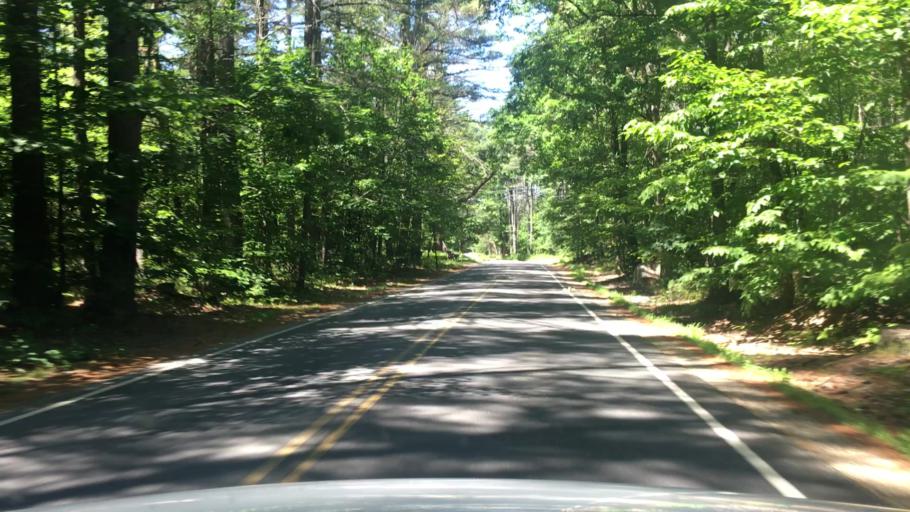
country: US
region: New Hampshire
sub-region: Merrimack County
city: Hopkinton
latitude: 43.2322
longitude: -71.6488
